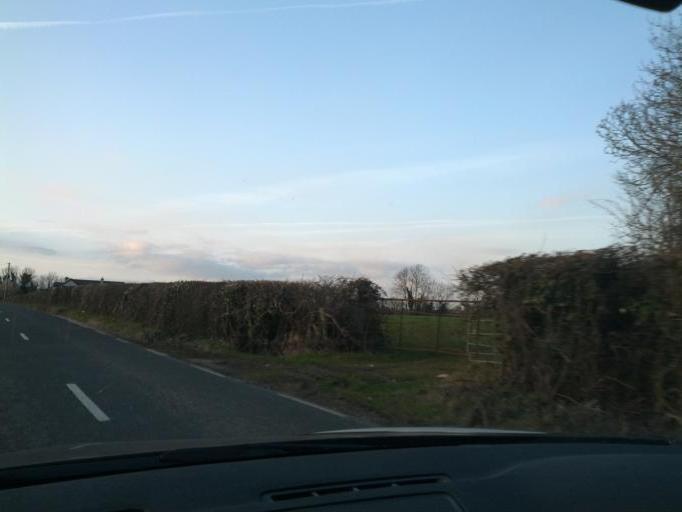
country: IE
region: Munster
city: Nenagh Bridge
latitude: 52.8968
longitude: -8.2059
